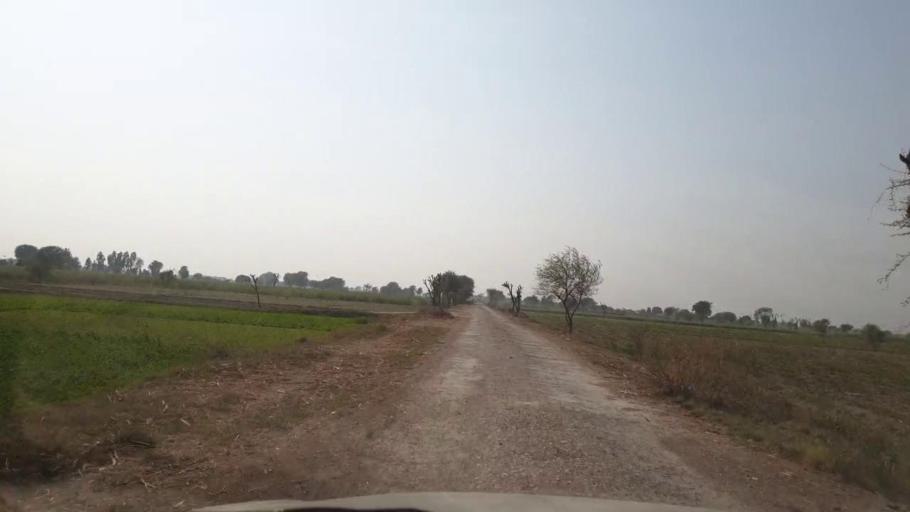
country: PK
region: Sindh
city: Pithoro
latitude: 25.6878
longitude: 69.2171
